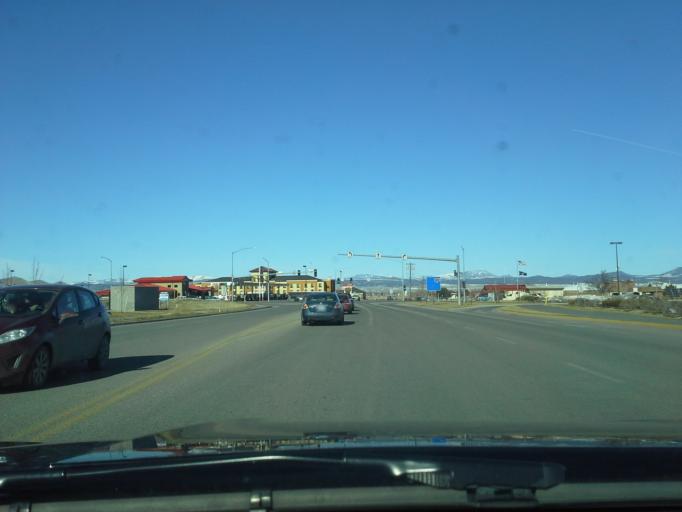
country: US
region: Montana
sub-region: Lewis and Clark County
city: Helena
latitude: 46.6151
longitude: -112.0048
